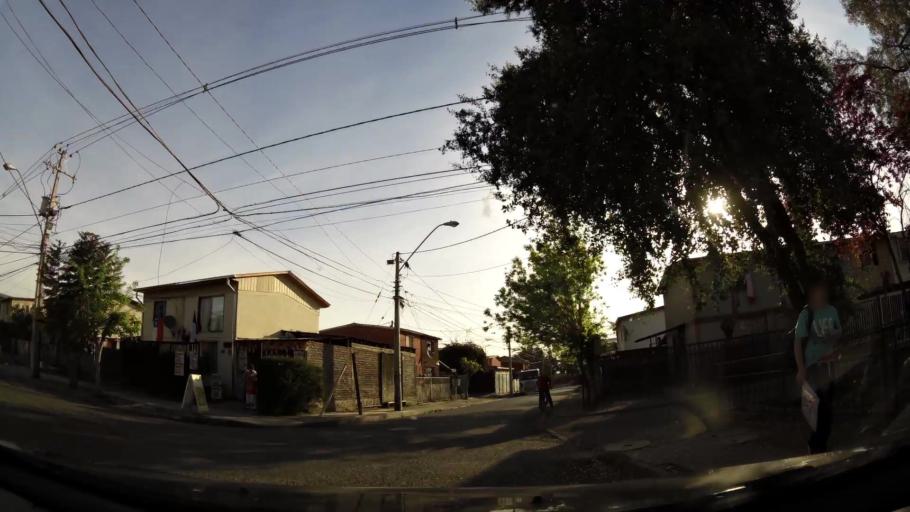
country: CL
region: Santiago Metropolitan
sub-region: Provincia de Cordillera
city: Puente Alto
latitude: -33.5954
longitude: -70.5680
